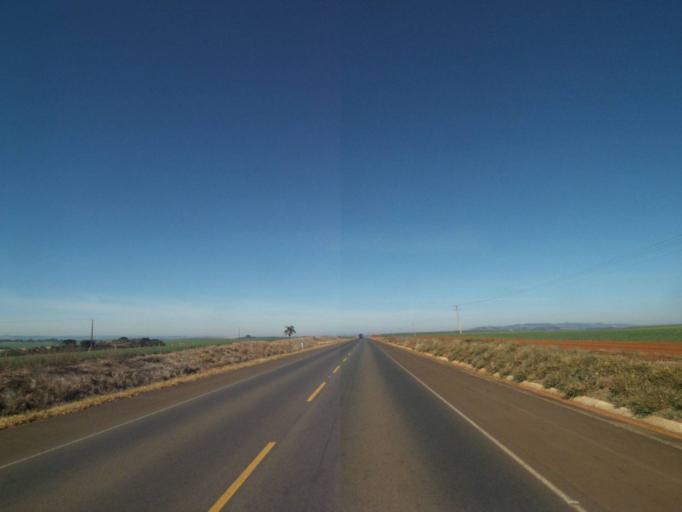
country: BR
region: Parana
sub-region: Tibagi
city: Tibagi
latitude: -24.4435
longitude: -50.4233
